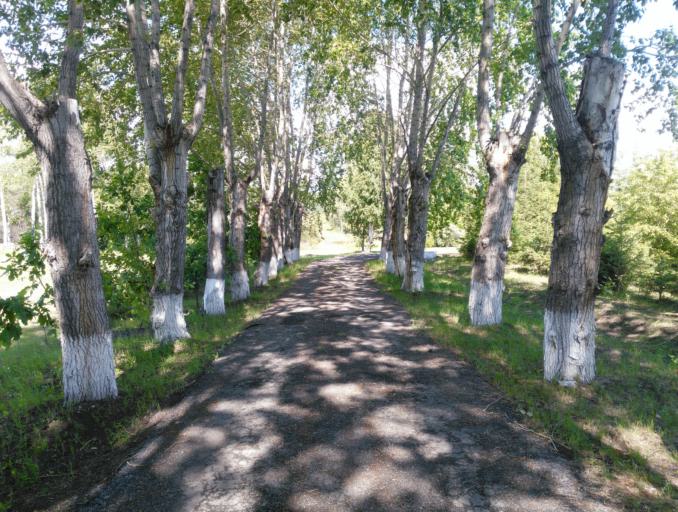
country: RU
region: Chelyabinsk
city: Chebarkul'
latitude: 54.9021
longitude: 60.2944
